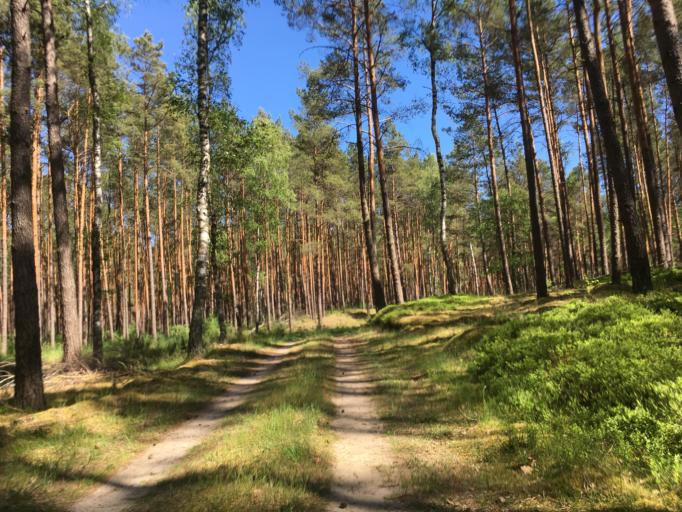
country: DE
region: Brandenburg
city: Friedrichswalde
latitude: 52.9667
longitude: 13.6477
